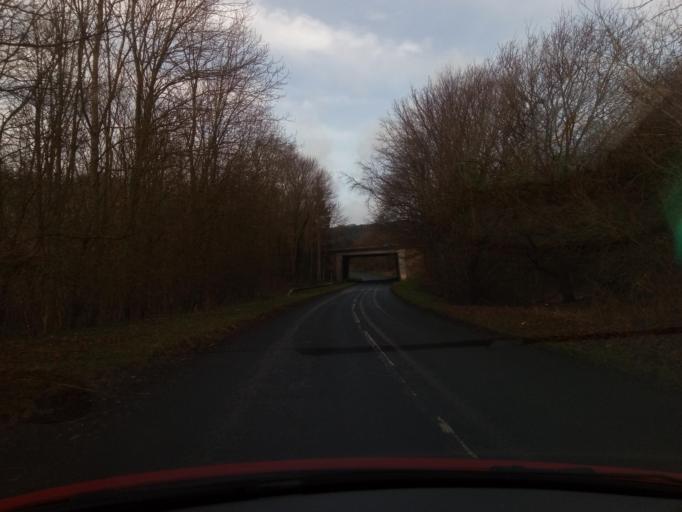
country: GB
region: England
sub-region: Northumberland
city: Corbridge
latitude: 54.9806
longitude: -2.0323
